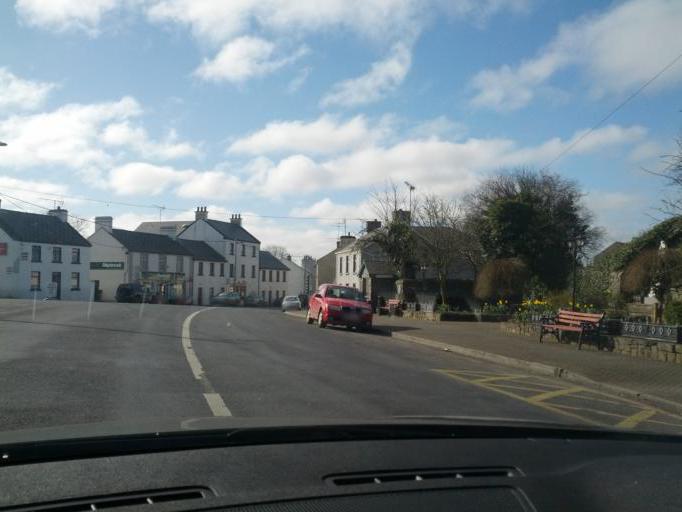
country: IE
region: Connaught
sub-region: County Galway
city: Ballinasloe
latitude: 53.3985
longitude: -8.3343
